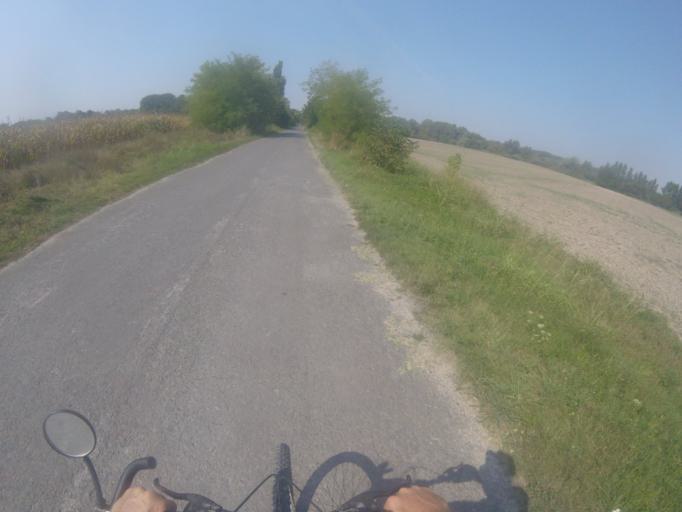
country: HU
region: Bacs-Kiskun
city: Ersekcsanad
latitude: 46.2573
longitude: 18.9259
